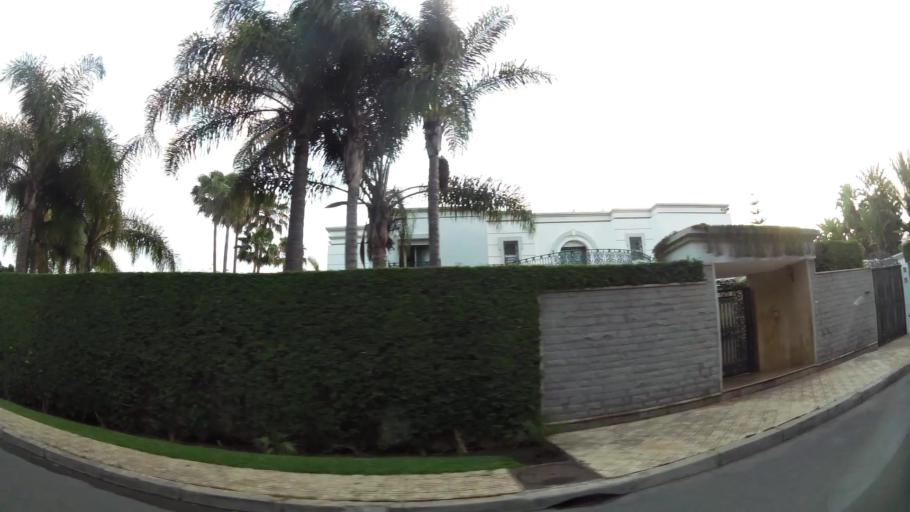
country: MA
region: Rabat-Sale-Zemmour-Zaer
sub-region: Rabat
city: Rabat
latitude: 33.9668
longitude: -6.8340
